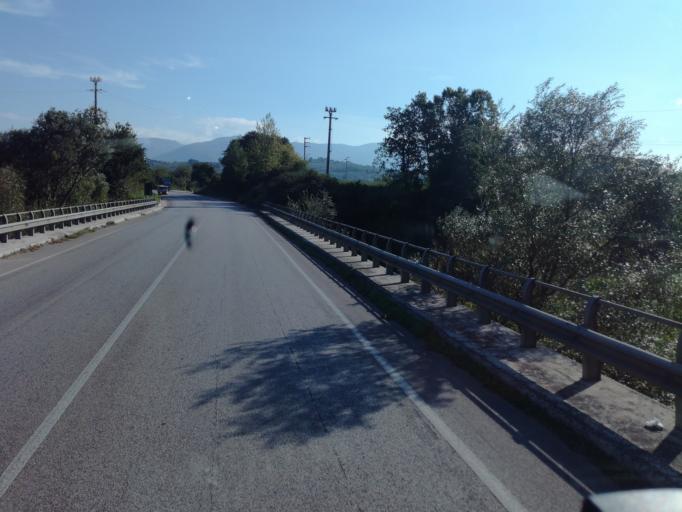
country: IT
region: Campania
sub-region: Provincia di Benevento
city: Dugenta
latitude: 41.1118
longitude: 14.4504
